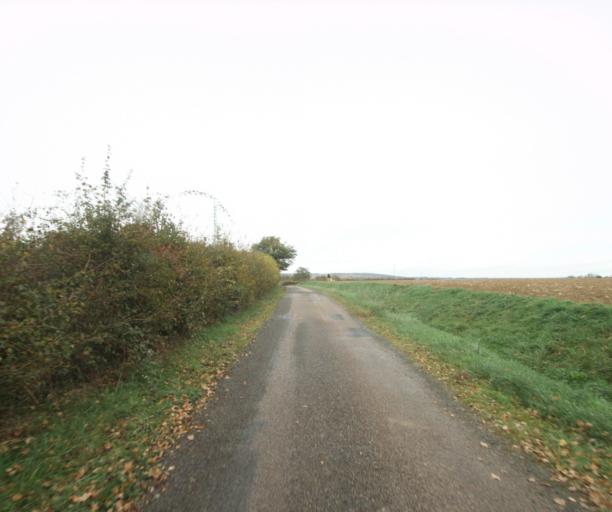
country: FR
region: Rhone-Alpes
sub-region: Departement de l'Ain
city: Pont-de-Vaux
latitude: 46.4664
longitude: 4.8724
